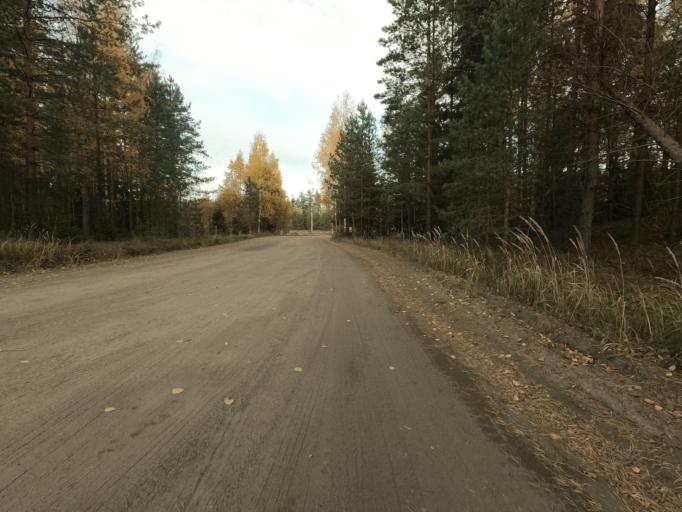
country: RU
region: Leningrad
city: Priladozhskiy
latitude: 59.6340
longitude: 31.3890
